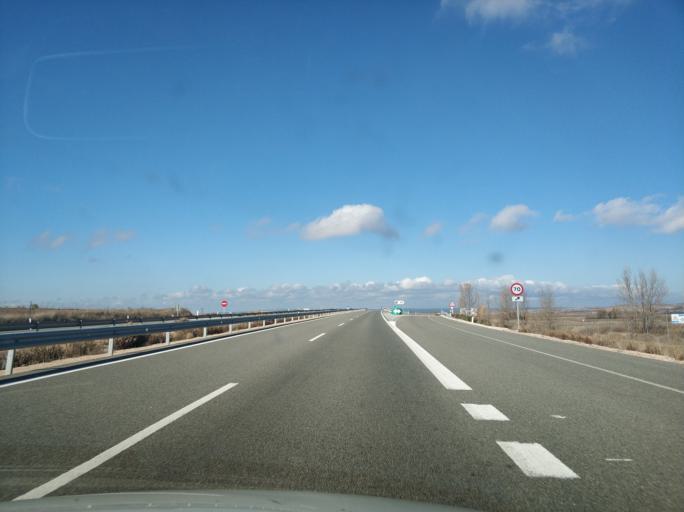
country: ES
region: Castille and Leon
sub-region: Provincia de Soria
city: Coscurita
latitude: 41.4169
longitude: -2.4876
